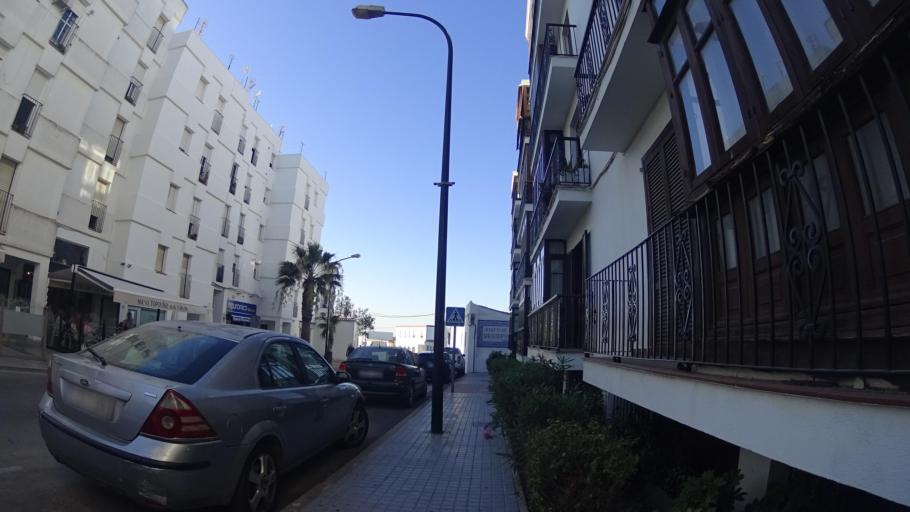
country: ES
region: Andalusia
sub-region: Provincia de Cadiz
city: Vejer de la Frontera
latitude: 36.2503
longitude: -5.9654
